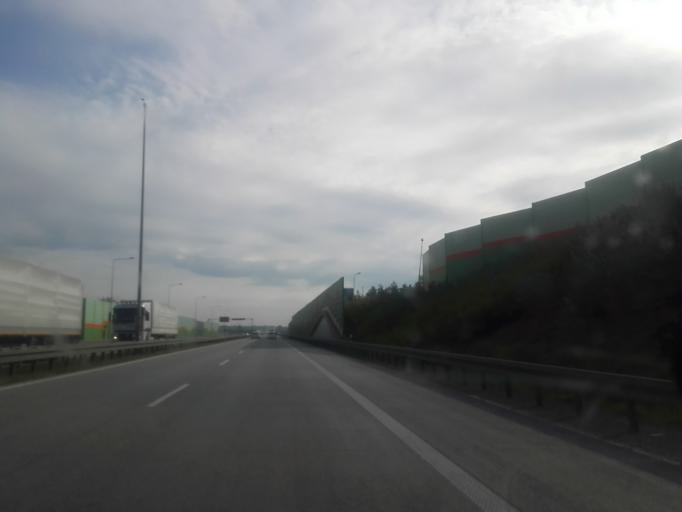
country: PL
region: Lodz Voivodeship
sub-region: Powiat tomaszowski
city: Tomaszow Mazowiecki
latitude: 51.5267
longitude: 19.9431
